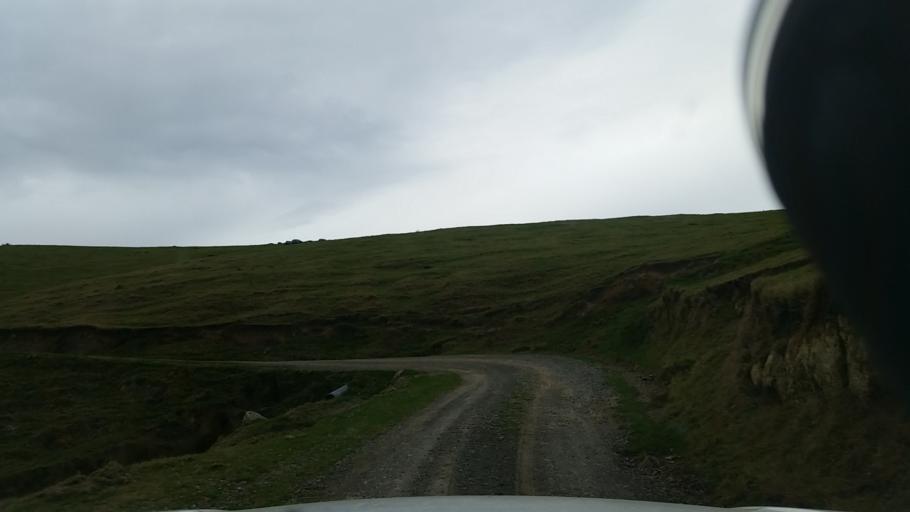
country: NZ
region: Canterbury
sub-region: Christchurch City
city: Christchurch
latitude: -43.8575
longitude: 173.0211
